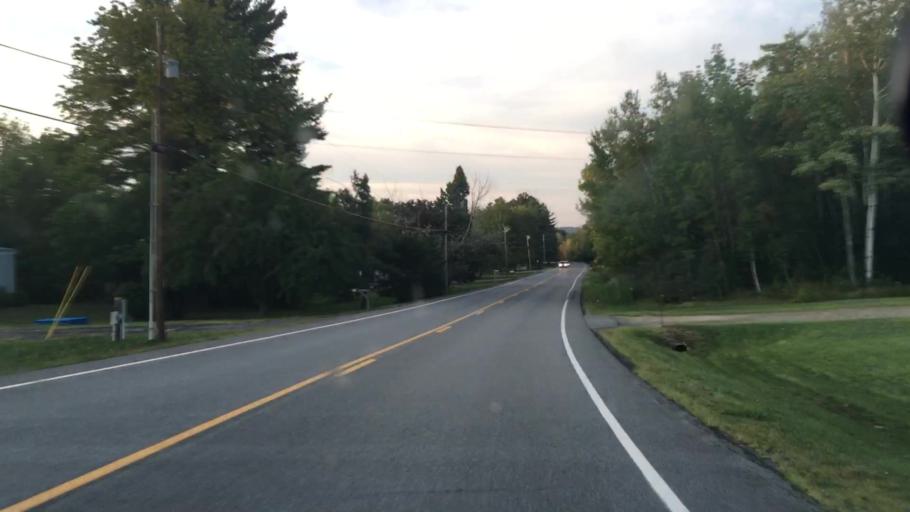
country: US
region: Maine
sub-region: Penobscot County
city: Hermon
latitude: 44.7408
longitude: -68.9665
